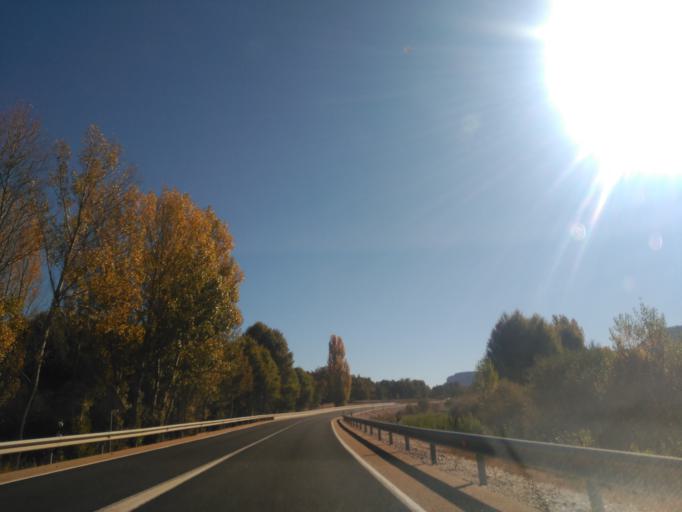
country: ES
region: Castille and Leon
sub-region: Provincia de Soria
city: Cidones
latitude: 41.8136
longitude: -2.7111
